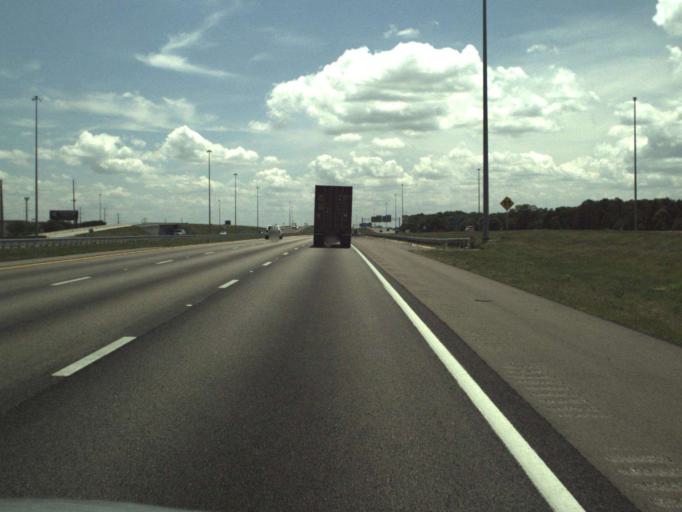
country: US
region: Florida
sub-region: Seminole County
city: Heathrow
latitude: 28.8044
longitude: -81.3417
